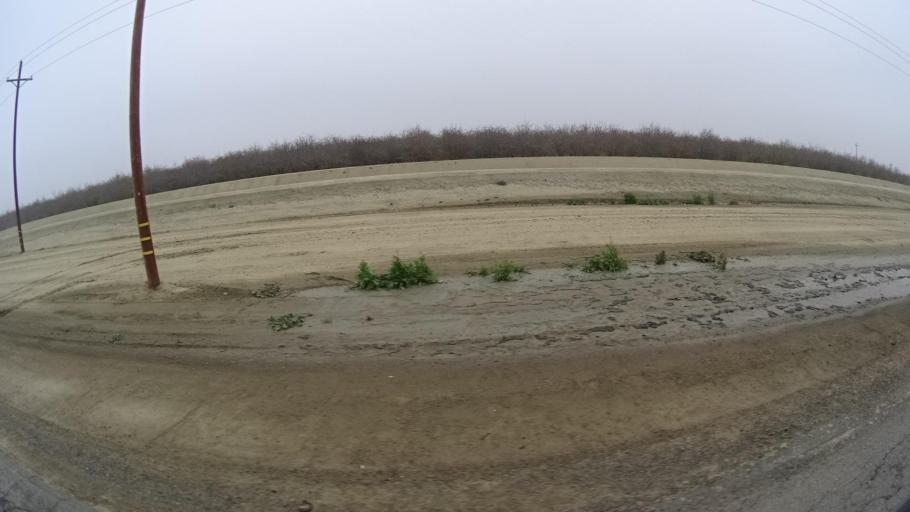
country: US
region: California
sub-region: Kern County
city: Wasco
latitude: 35.6897
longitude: -119.4017
